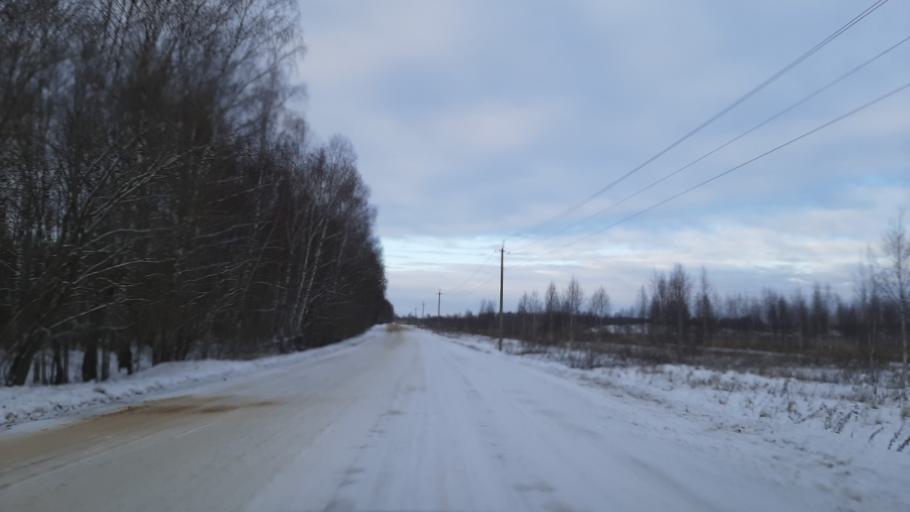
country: RU
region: Kostroma
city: Nerekhta
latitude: 57.4718
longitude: 40.6690
